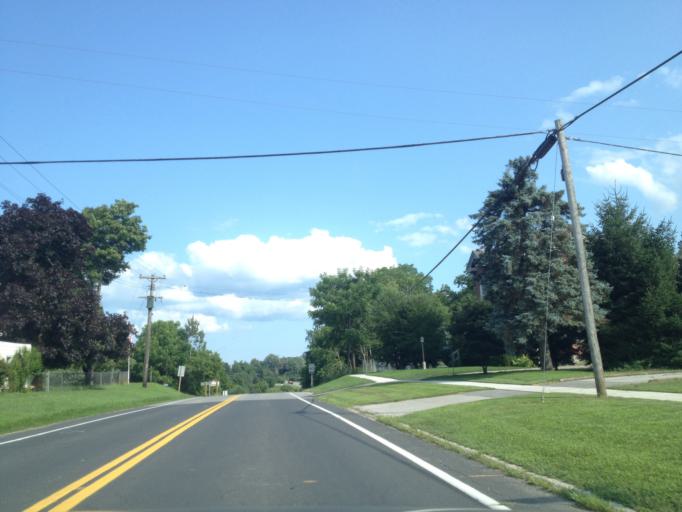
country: CA
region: Ontario
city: Aylmer
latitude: 42.7638
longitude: -80.8439
